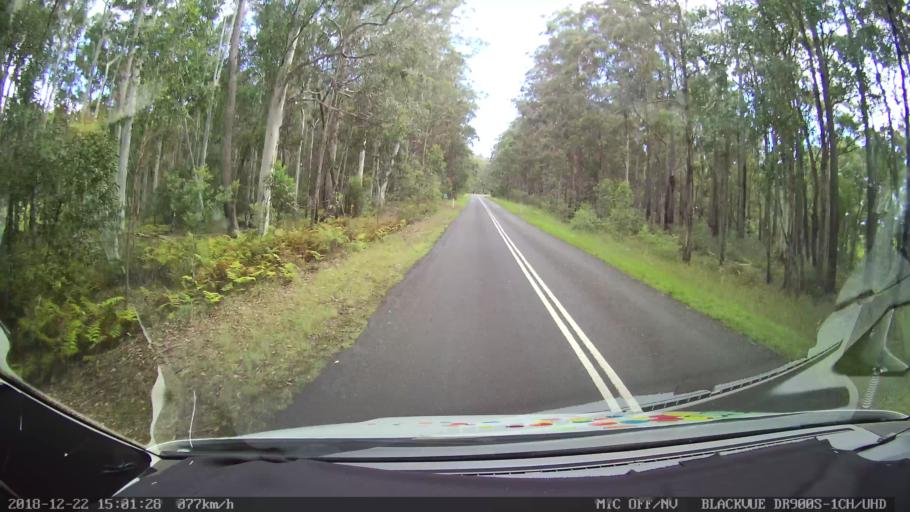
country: AU
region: New South Wales
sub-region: Bellingen
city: Dorrigo
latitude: -30.2548
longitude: 152.4585
